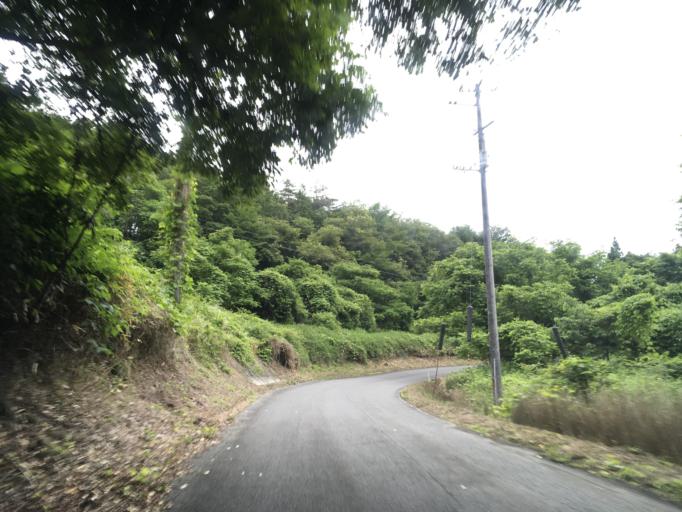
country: JP
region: Iwate
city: Ichinoseki
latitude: 38.8481
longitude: 141.3224
